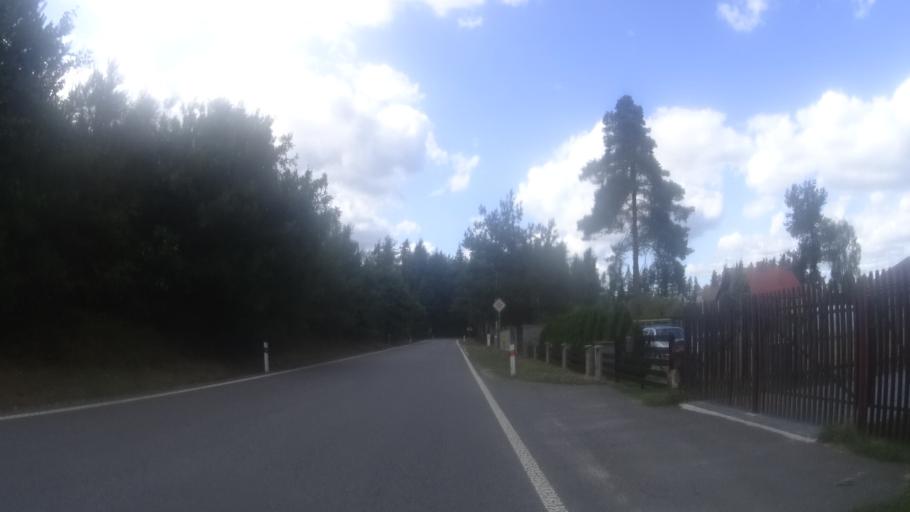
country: CZ
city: Borohradek
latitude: 50.0782
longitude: 16.1243
